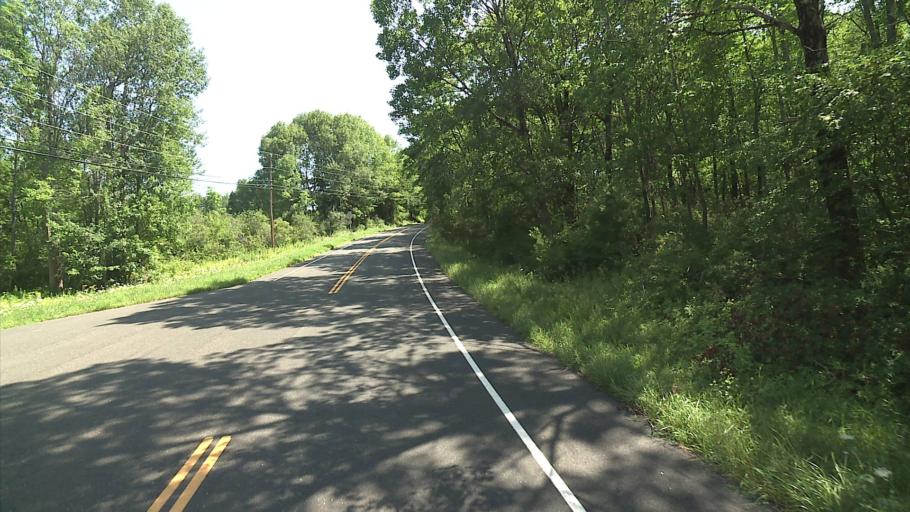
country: US
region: Massachusetts
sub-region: Berkshire County
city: New Marlborough
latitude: 42.0095
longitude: -73.2029
